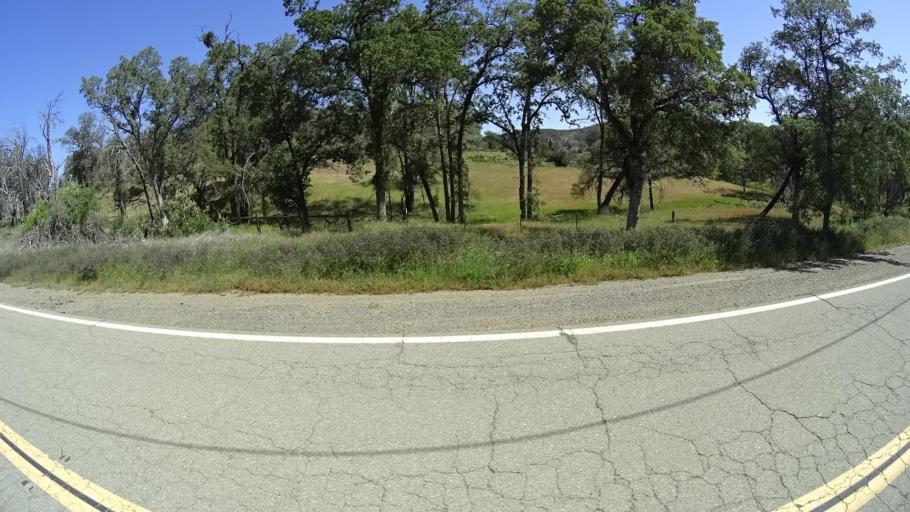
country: US
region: California
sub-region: Lake County
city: Hidden Valley Lake
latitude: 38.8812
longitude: -122.4490
